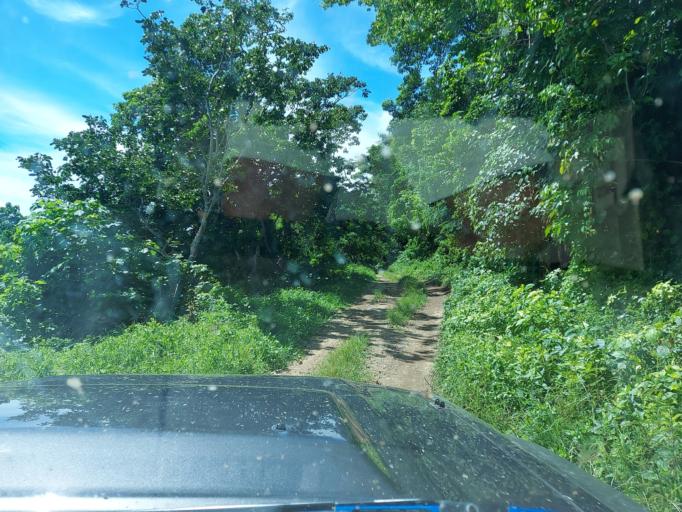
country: VU
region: Malampa
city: Lakatoro
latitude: -16.3297
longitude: 167.7331
